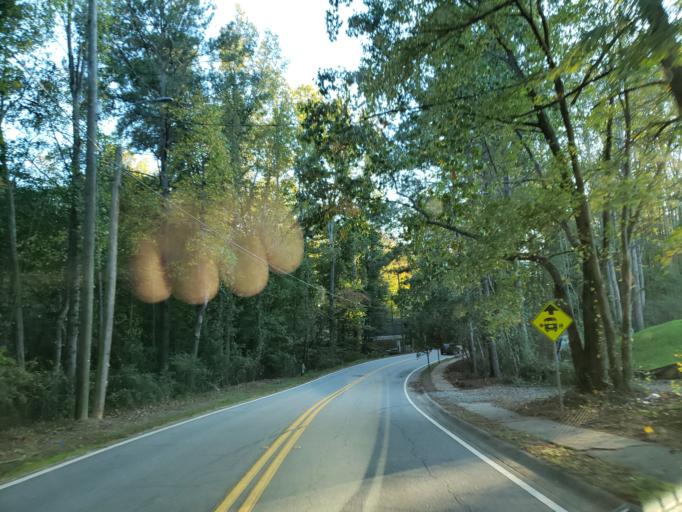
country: US
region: Georgia
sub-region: Fulton County
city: Roswell
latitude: 33.9891
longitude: -84.4375
